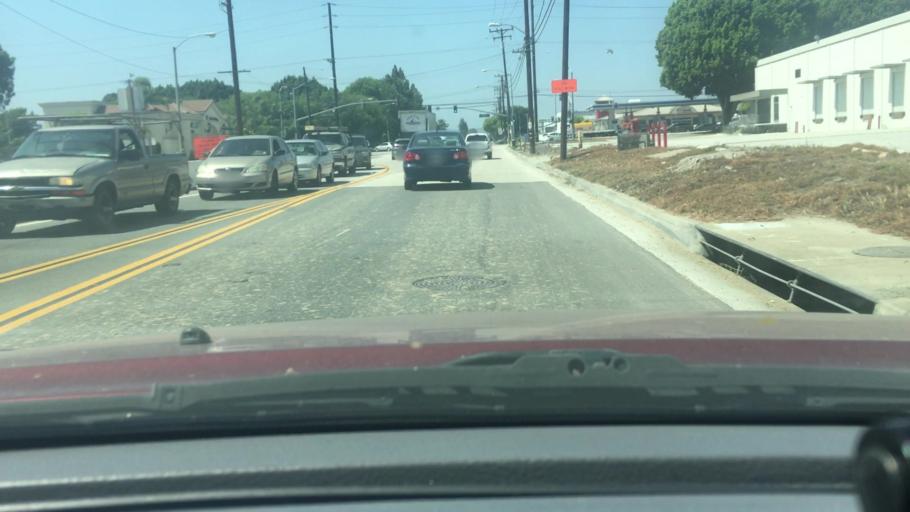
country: US
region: California
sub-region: Los Angeles County
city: La Mirada
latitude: 33.8868
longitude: -118.0289
